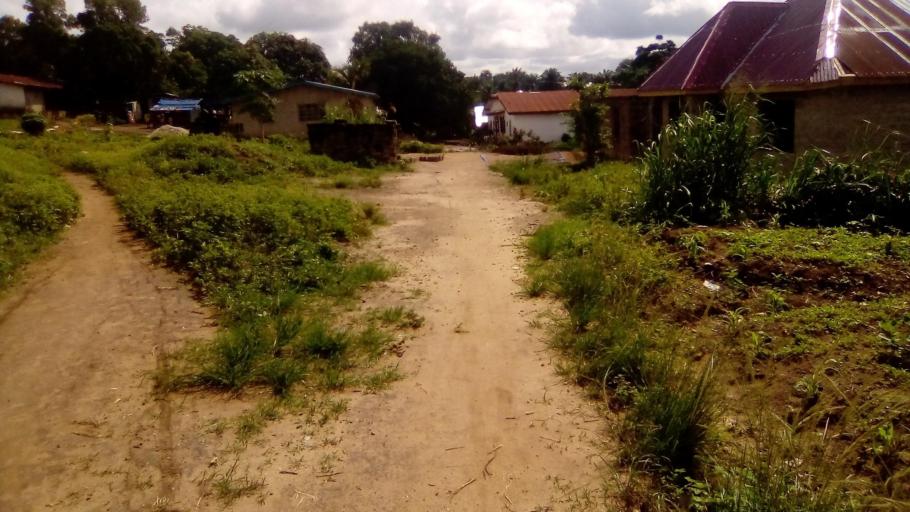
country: SL
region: Southern Province
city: Bo
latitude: 7.9772
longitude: -11.7250
